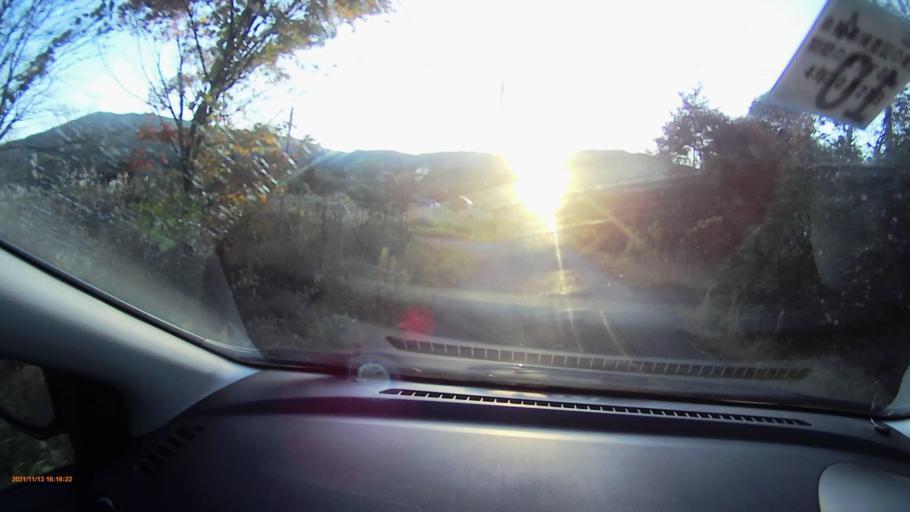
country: JP
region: Gifu
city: Nakatsugawa
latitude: 35.5769
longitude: 137.5088
